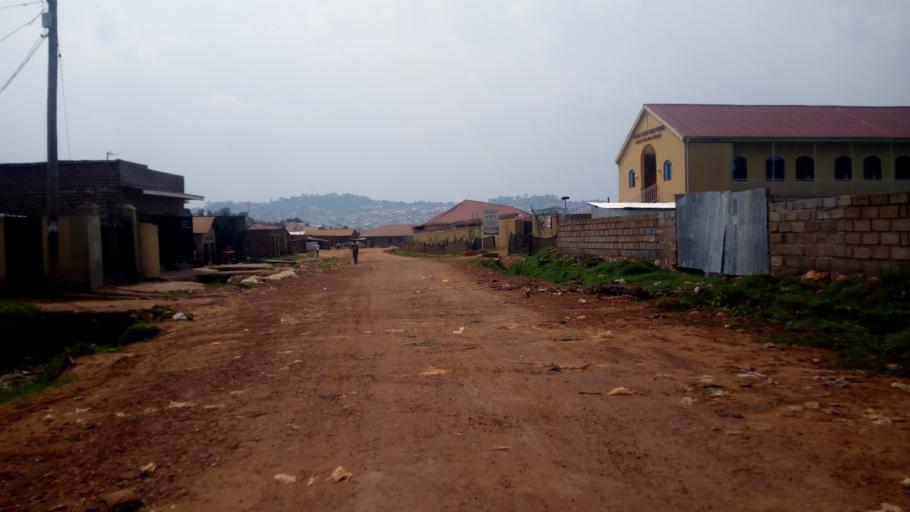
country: UG
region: Central Region
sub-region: Wakiso District
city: Kireka
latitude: 0.3182
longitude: 32.6526
